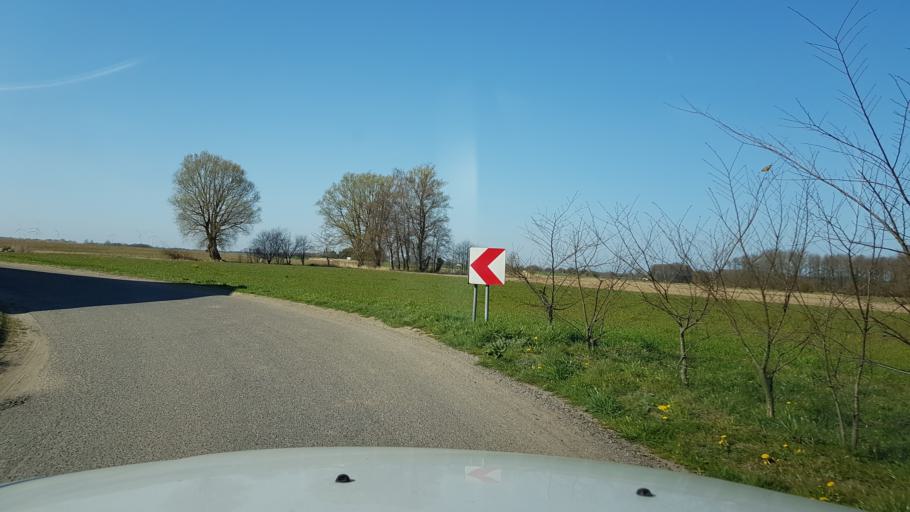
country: PL
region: West Pomeranian Voivodeship
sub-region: Powiat kolobrzeski
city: Ustronie Morskie
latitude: 54.2366
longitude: 15.8728
